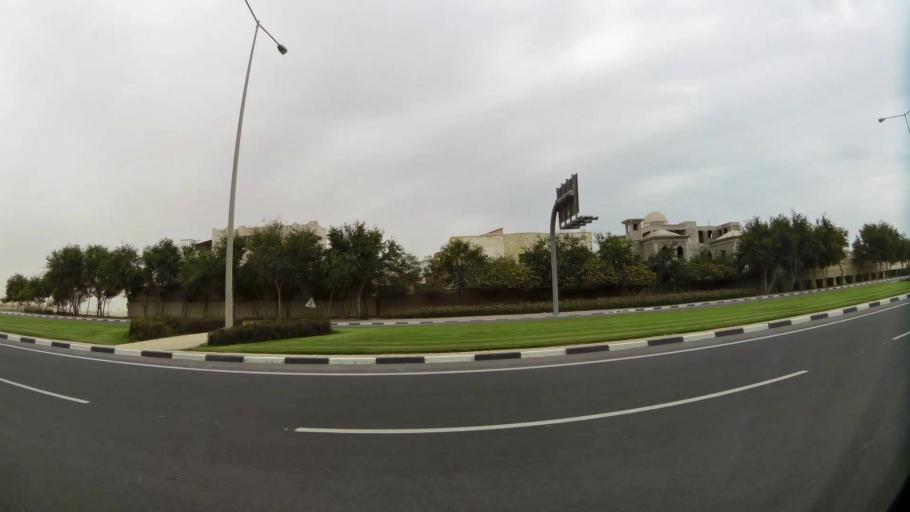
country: QA
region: Baladiyat ad Dawhah
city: Doha
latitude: 25.3484
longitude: 51.4931
